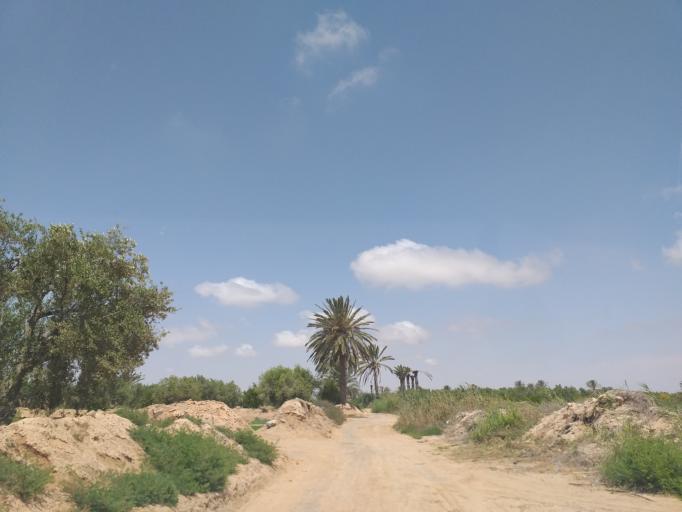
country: TN
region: Qabis
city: Gabes
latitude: 33.9510
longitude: 10.0499
